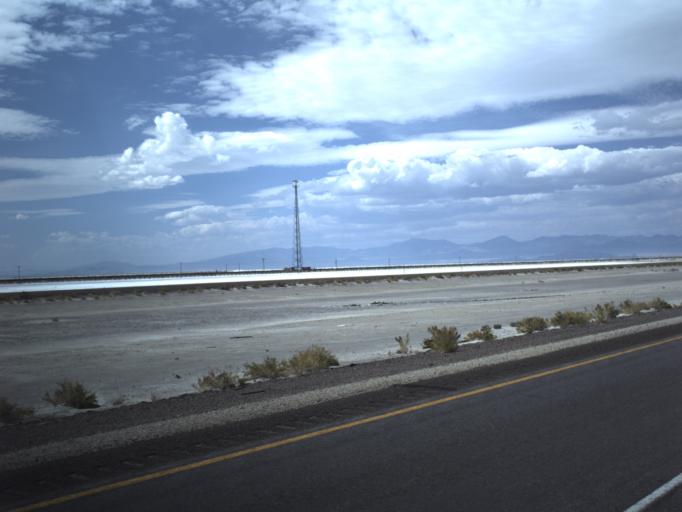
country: US
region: Utah
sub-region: Tooele County
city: Wendover
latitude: 40.7380
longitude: -113.7813
